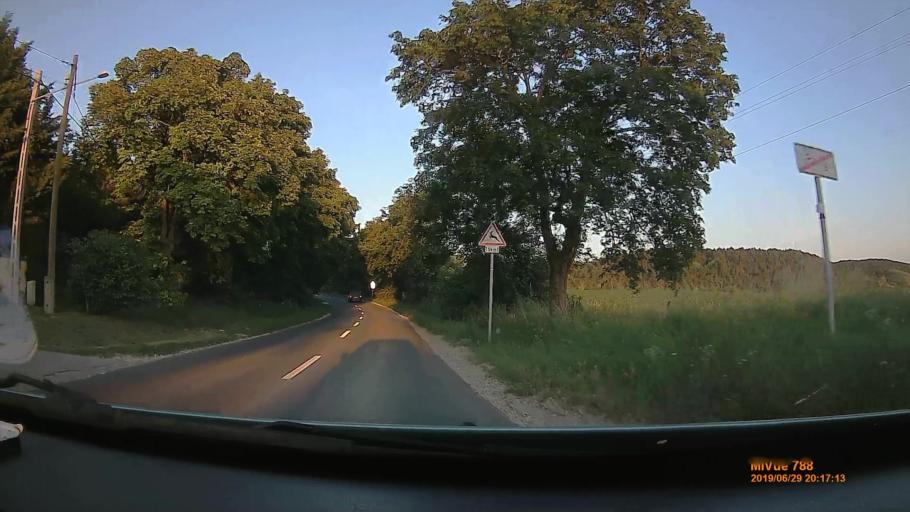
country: HU
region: Pest
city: Paty
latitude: 47.5099
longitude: 18.8438
